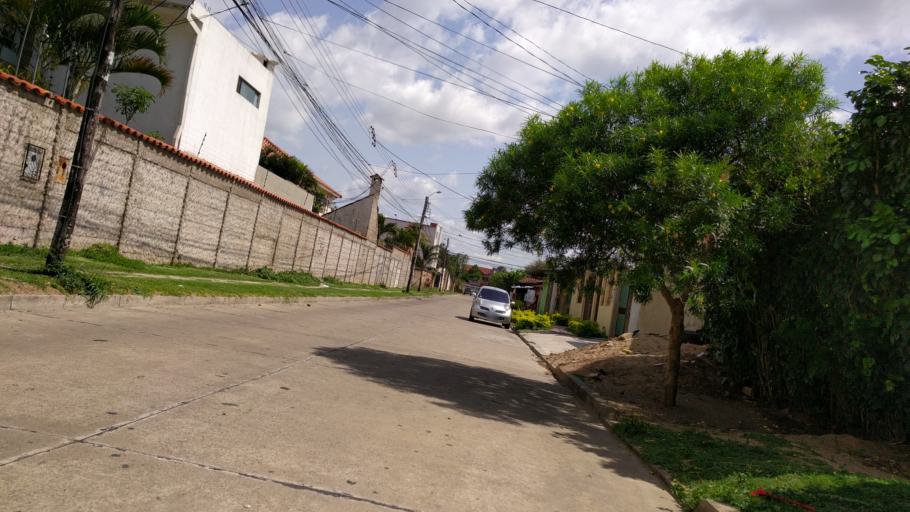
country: BO
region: Santa Cruz
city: Santa Cruz de la Sierra
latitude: -17.7773
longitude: -63.2111
